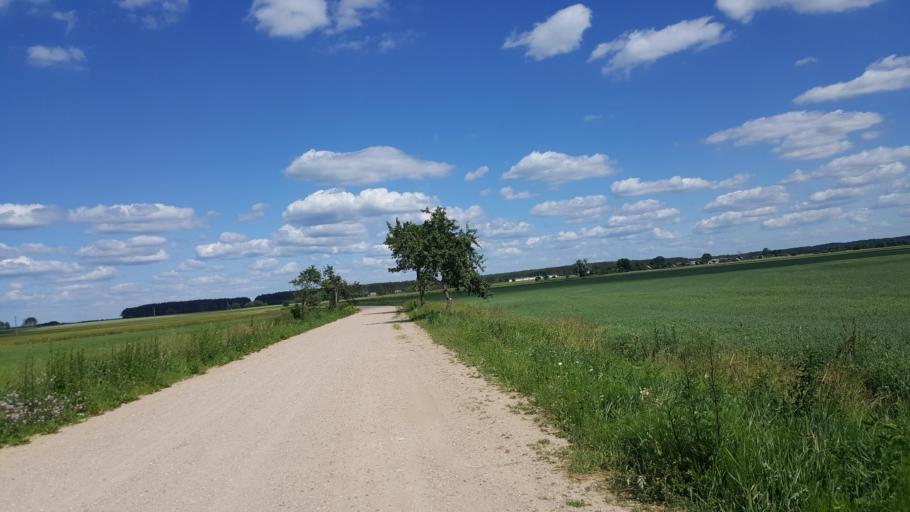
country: PL
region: Podlasie
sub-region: Powiat hajnowski
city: Hajnowka
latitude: 52.5423
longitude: 23.5807
